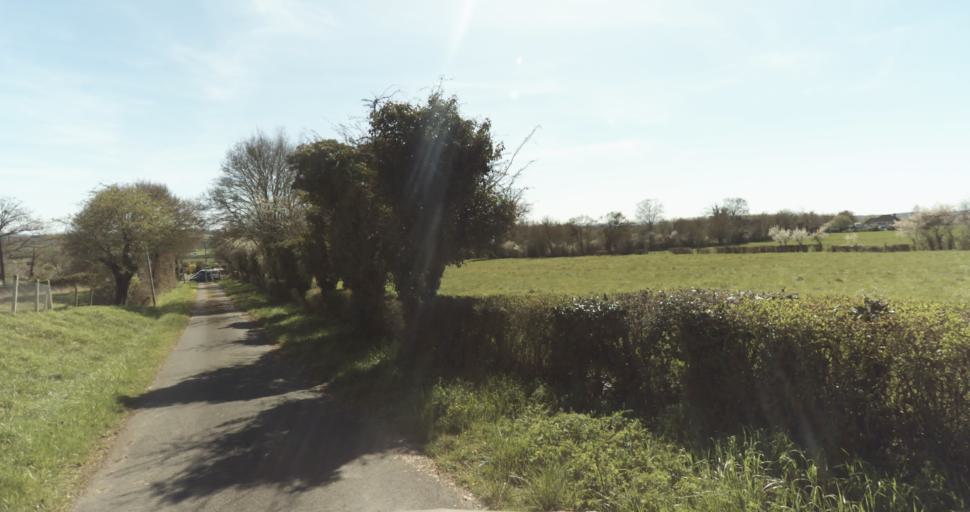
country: FR
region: Lower Normandy
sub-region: Departement du Calvados
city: Saint-Pierre-sur-Dives
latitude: 49.0517
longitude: -0.0159
